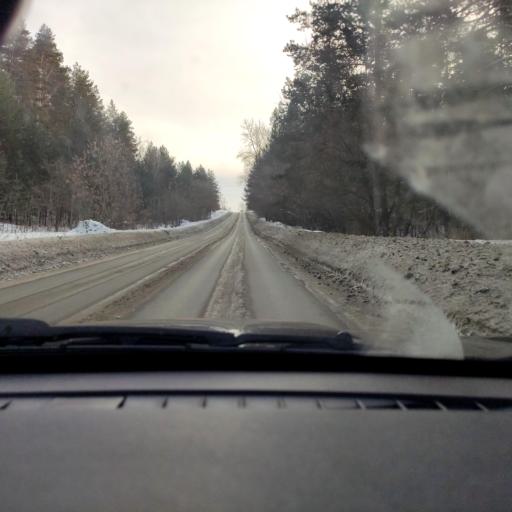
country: RU
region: Samara
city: Pribrezhnyy
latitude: 53.5007
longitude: 49.8489
